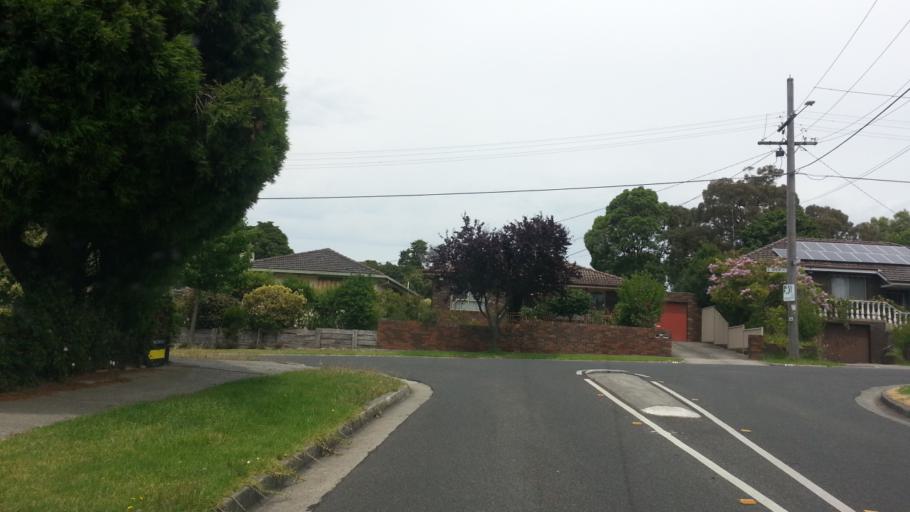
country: AU
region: Victoria
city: Mitcham
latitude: -37.8268
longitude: 145.2019
